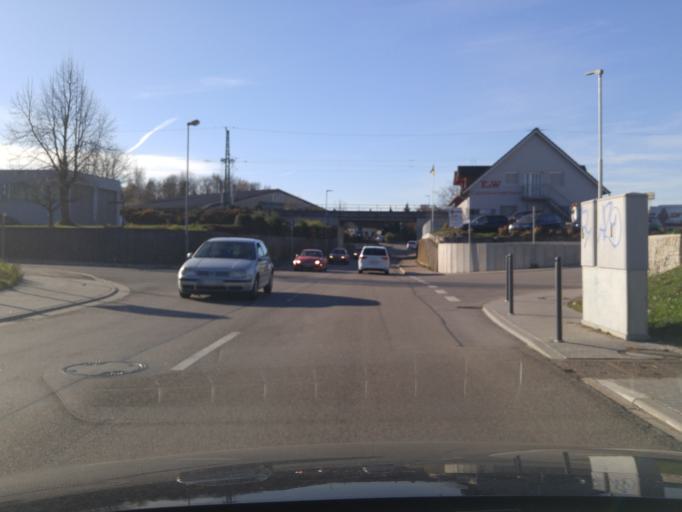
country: DE
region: Baden-Wuerttemberg
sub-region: Karlsruhe Region
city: Sinsheim
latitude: 49.2404
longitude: 8.9036
